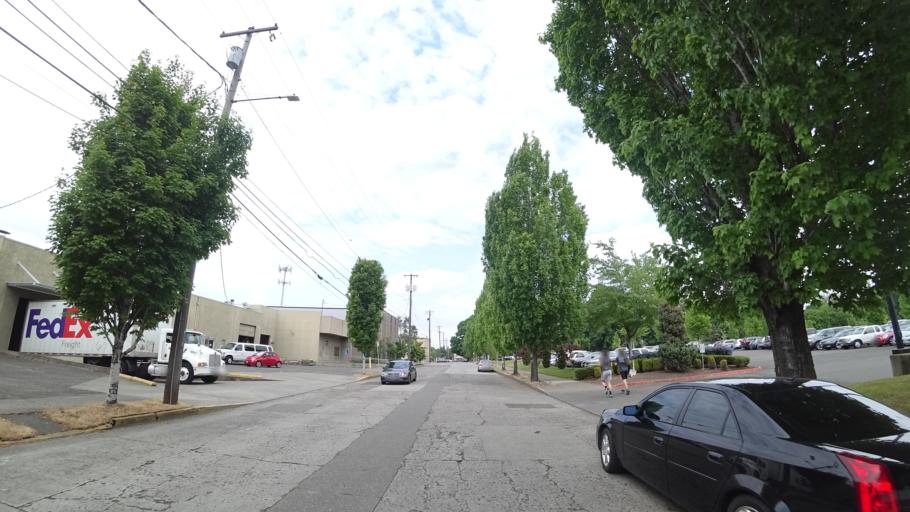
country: US
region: Oregon
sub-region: Multnomah County
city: Portland
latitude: 45.4961
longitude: -122.6435
